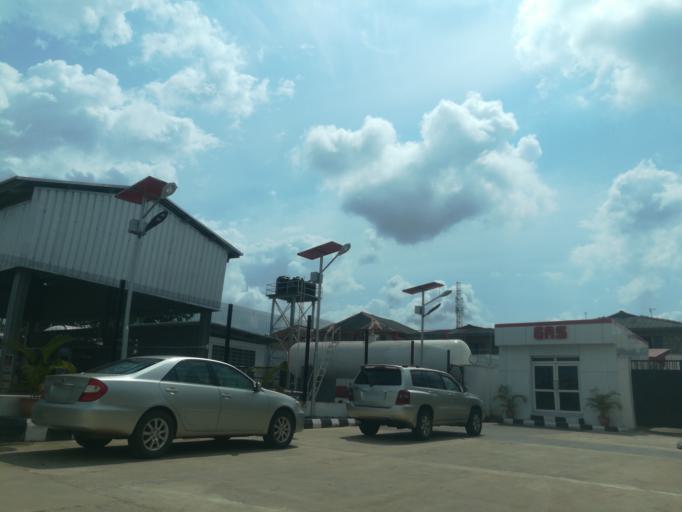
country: NG
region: Oyo
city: Ibadan
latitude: 7.3645
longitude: 3.8851
